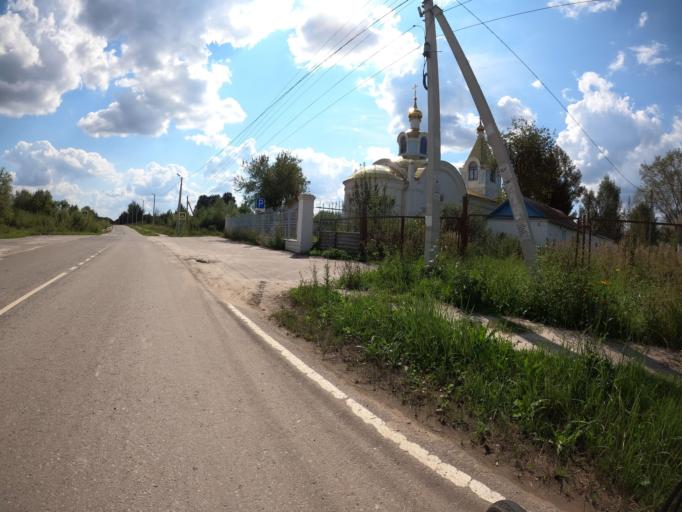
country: RU
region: Moskovskaya
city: Troitskoye
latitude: 55.2568
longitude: 38.5782
